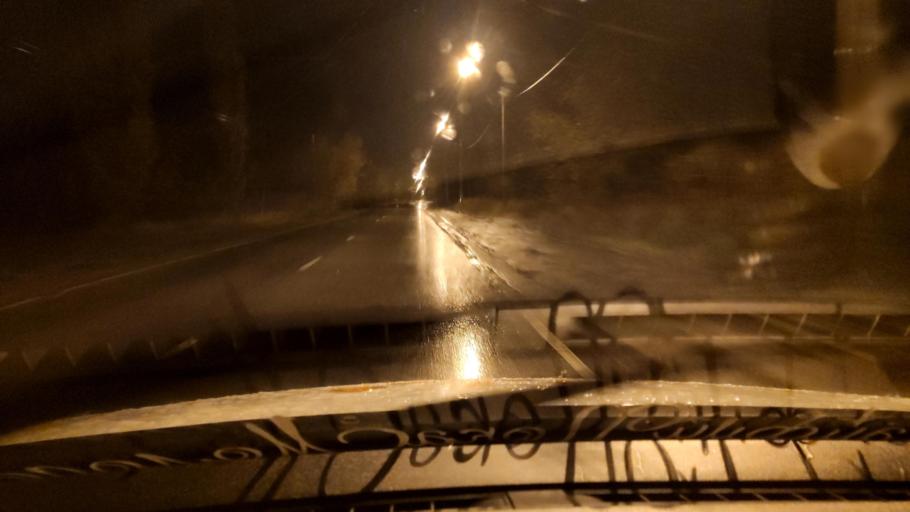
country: RU
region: Voronezj
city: Somovo
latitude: 51.7255
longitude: 39.2962
